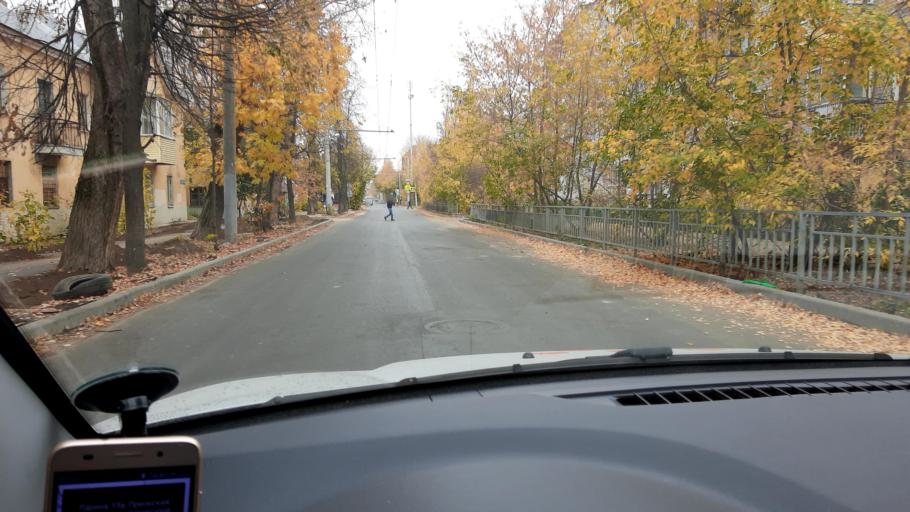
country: RU
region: Nizjnij Novgorod
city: Gorbatovka
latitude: 56.2877
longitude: 43.8488
